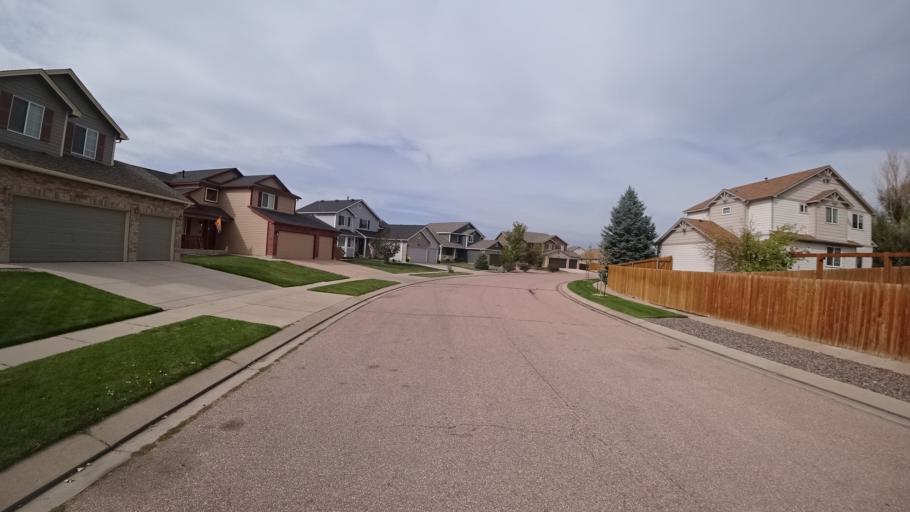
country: US
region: Colorado
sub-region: El Paso County
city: Cimarron Hills
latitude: 38.9185
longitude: -104.7096
